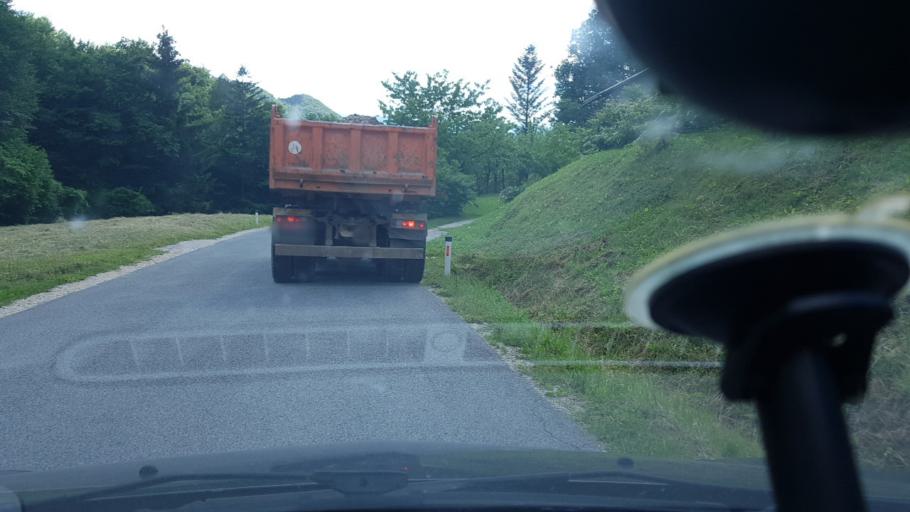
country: SI
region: Rogatec
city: Rogatec
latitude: 46.2567
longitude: 15.7550
